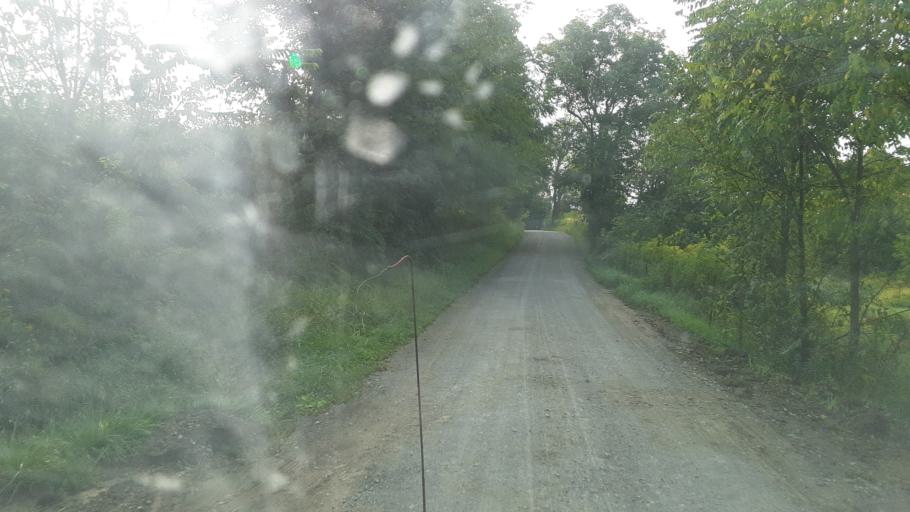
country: US
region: Ohio
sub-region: Holmes County
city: Millersburg
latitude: 40.4361
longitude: -81.8309
